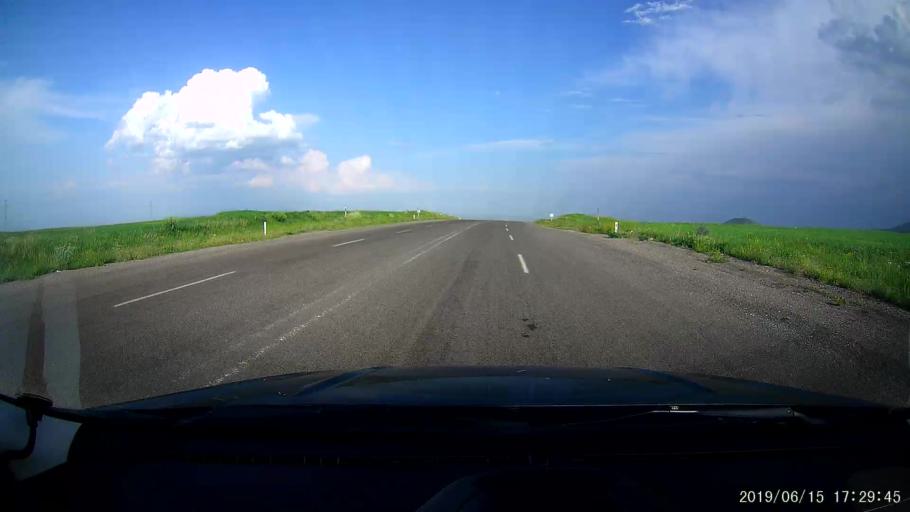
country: TR
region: Kars
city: Basgedikler
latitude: 40.5875
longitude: 43.4575
